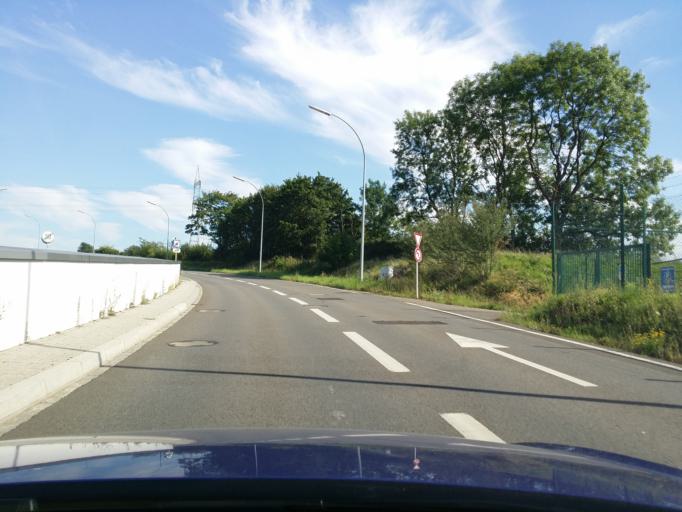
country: LU
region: Luxembourg
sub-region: Canton de Luxembourg
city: Bertrange
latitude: 49.6216
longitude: 6.0386
